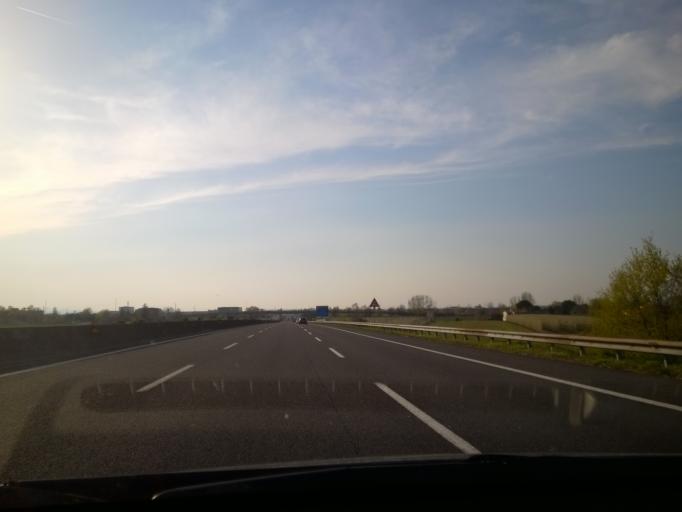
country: IT
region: Emilia-Romagna
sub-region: Provincia di Ravenna
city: Granarolo
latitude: 44.3217
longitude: 11.9105
